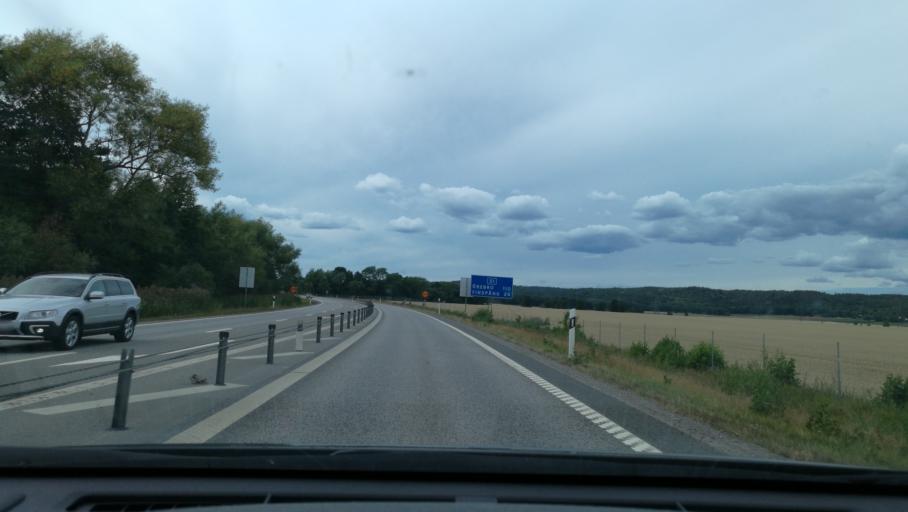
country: SE
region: OEstergoetland
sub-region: Norrkopings Kommun
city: Jursla
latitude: 58.6315
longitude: 16.1417
